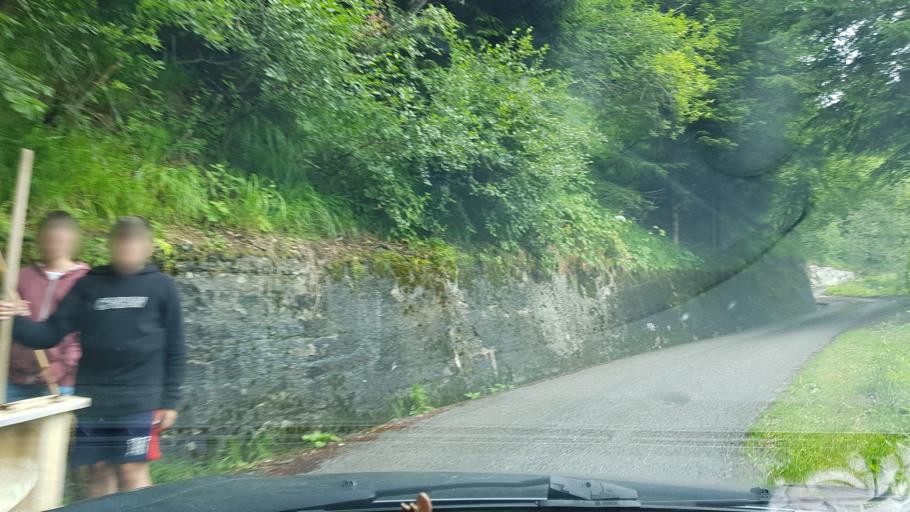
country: IT
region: Friuli Venezia Giulia
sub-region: Provincia di Udine
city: Cercivento
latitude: 46.5470
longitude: 12.9801
